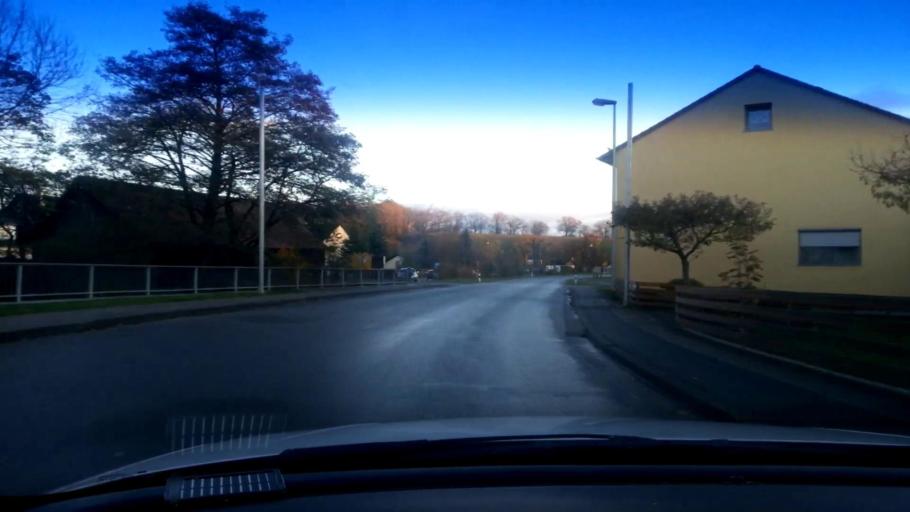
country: DE
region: Bavaria
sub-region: Upper Franconia
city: Buttenheim
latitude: 49.8019
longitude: 11.0330
